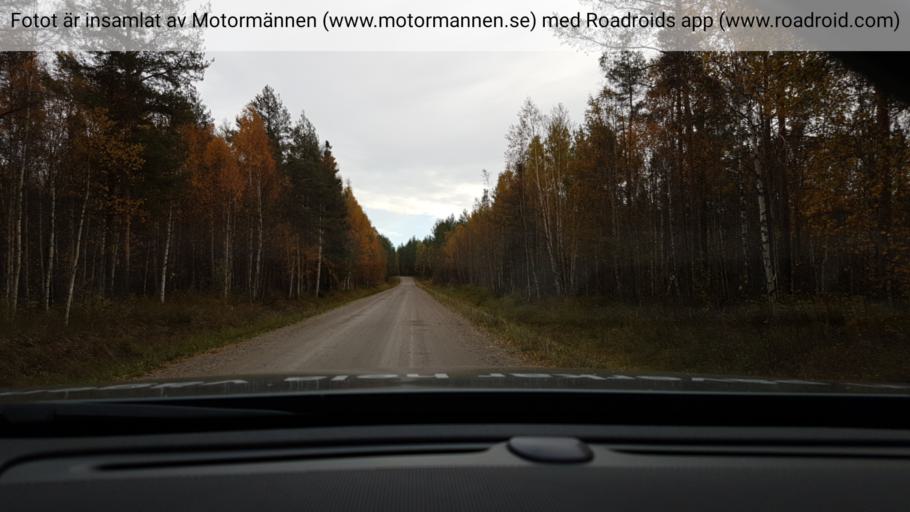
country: SE
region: Norrbotten
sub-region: Overkalix Kommun
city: OEverkalix
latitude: 66.2934
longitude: 22.9498
